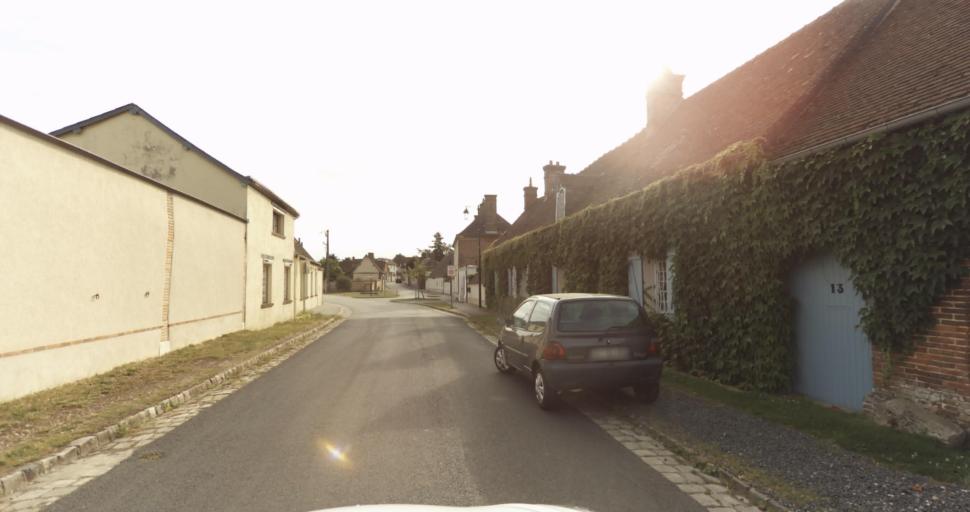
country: FR
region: Haute-Normandie
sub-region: Departement de l'Eure
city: Saint-Germain-sur-Avre
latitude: 48.8203
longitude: 1.2644
